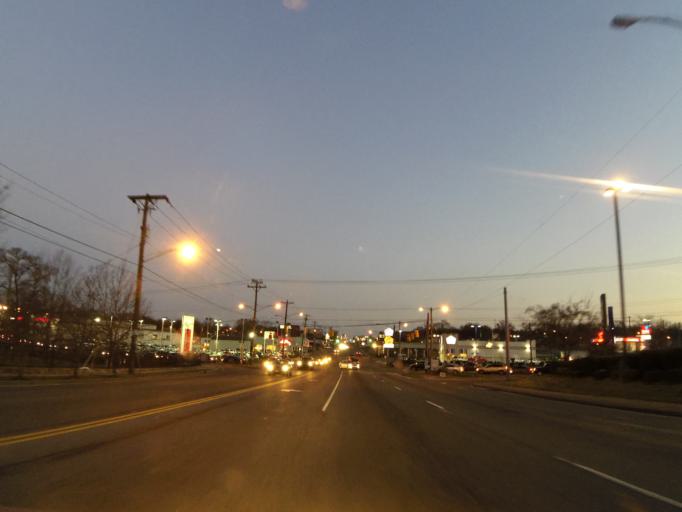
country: US
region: Tennessee
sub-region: Davidson County
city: Oak Hill
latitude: 36.1117
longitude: -86.7457
